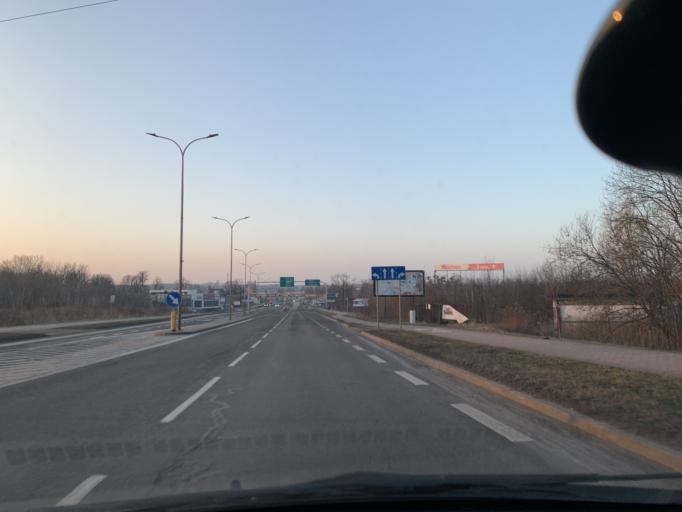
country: PL
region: Silesian Voivodeship
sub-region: Piekary Slaskie
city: Piekary Slaskie
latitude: 50.3656
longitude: 18.8995
